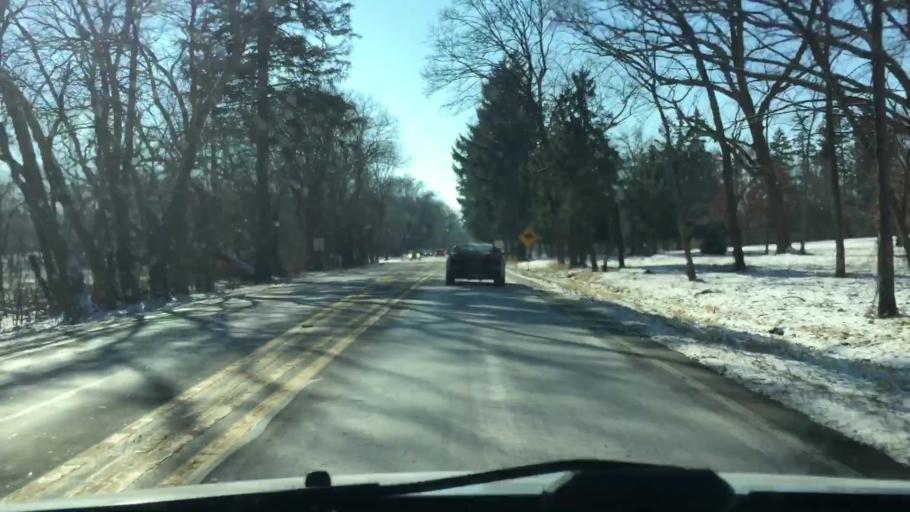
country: US
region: Illinois
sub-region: DuPage County
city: Wayne
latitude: 41.9526
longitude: -88.2693
